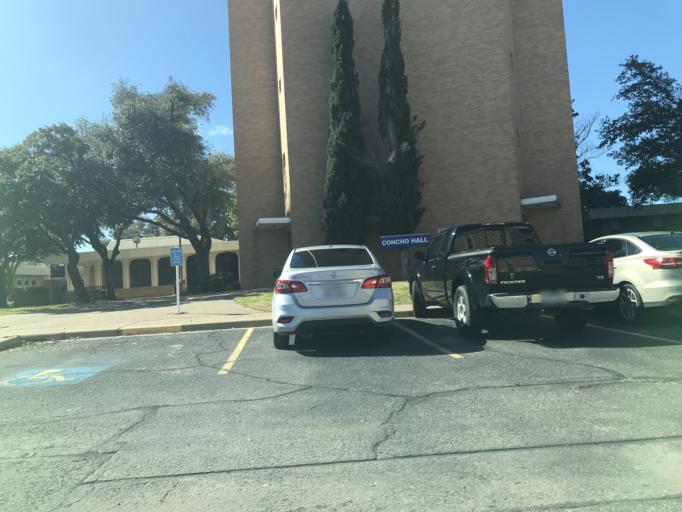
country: US
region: Texas
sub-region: Tom Green County
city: San Angelo
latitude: 31.4410
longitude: -100.4585
